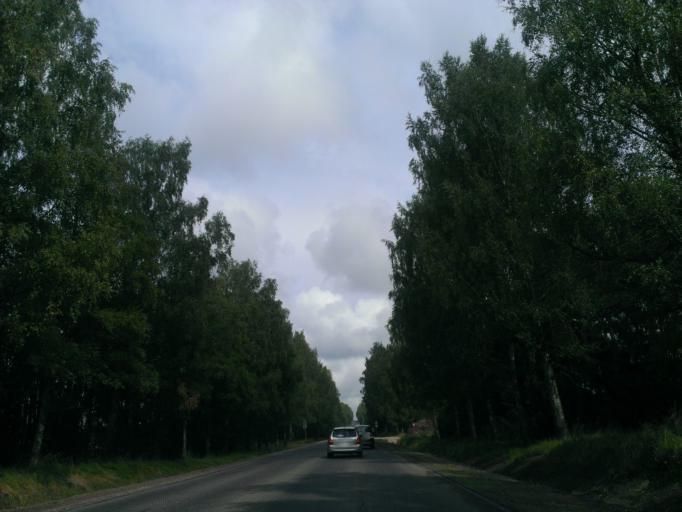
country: LV
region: Ligatne
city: Ligatne
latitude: 57.1934
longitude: 25.0851
